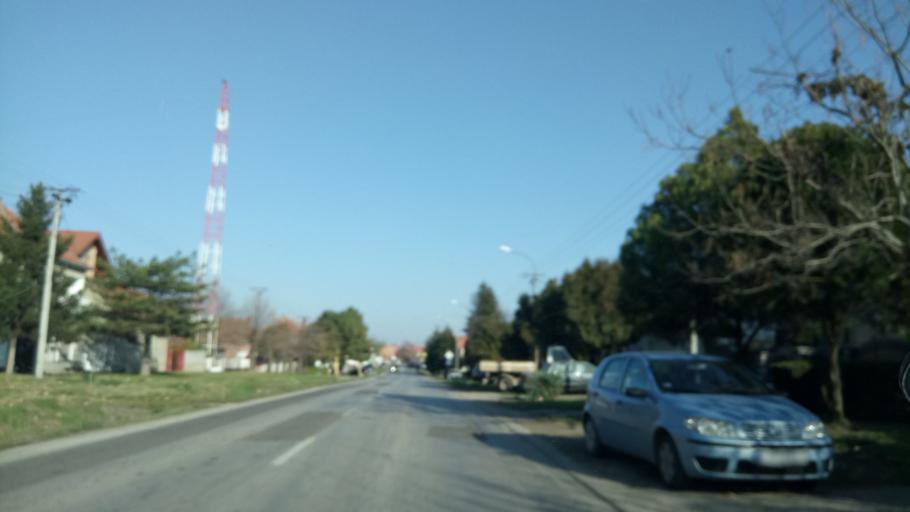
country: RS
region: Autonomna Pokrajina Vojvodina
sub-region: Sremski Okrug
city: Ingija
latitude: 45.0423
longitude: 20.0728
